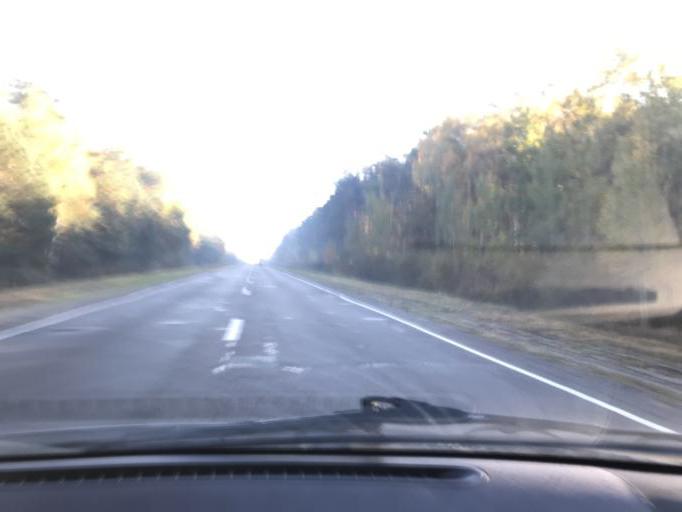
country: BY
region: Brest
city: Asnyezhytsy
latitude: 52.2488
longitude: 26.2483
